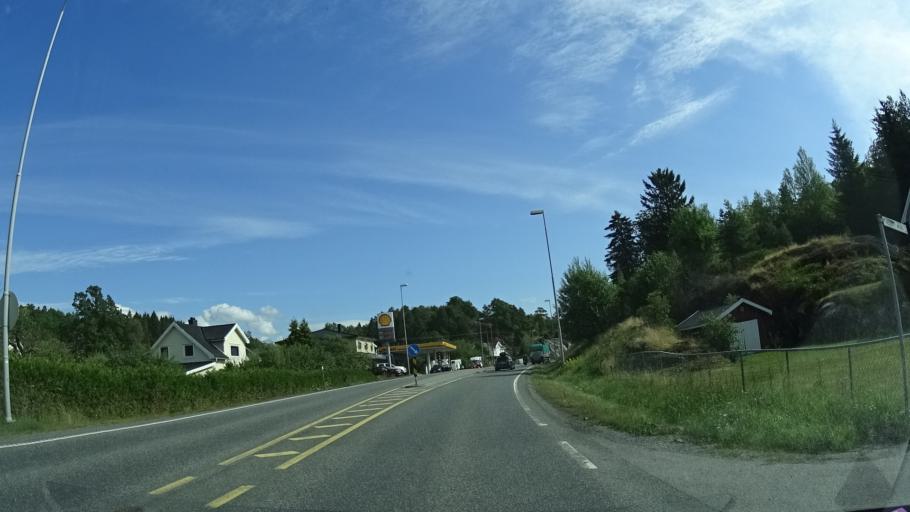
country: NO
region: Telemark
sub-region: Bamble
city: Langesund
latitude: 59.0115
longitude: 9.6656
